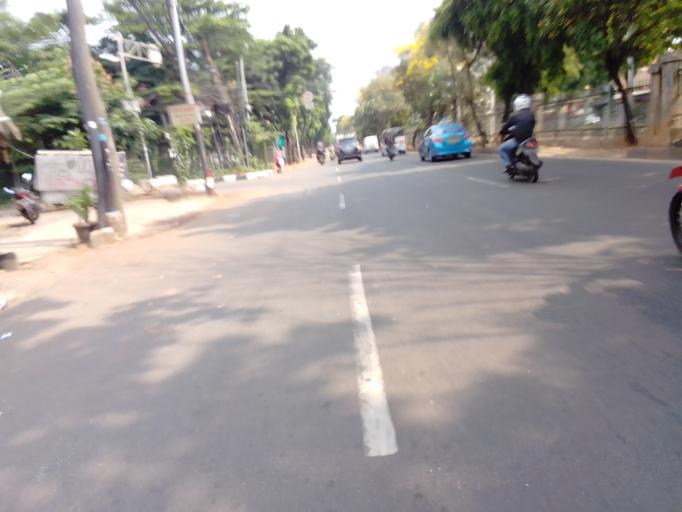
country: ID
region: Jakarta Raya
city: Jakarta
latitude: -6.2187
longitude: 106.7923
